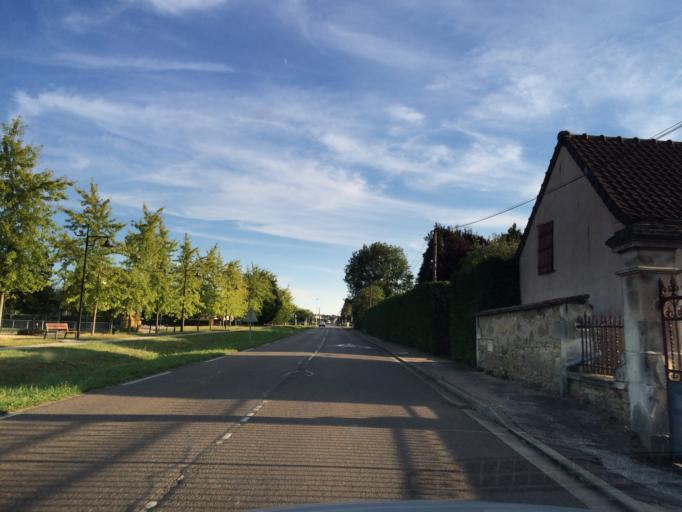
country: FR
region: Bourgogne
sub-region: Departement de l'Yonne
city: Saint-Georges-sur-Baulche
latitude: 47.8235
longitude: 3.5395
